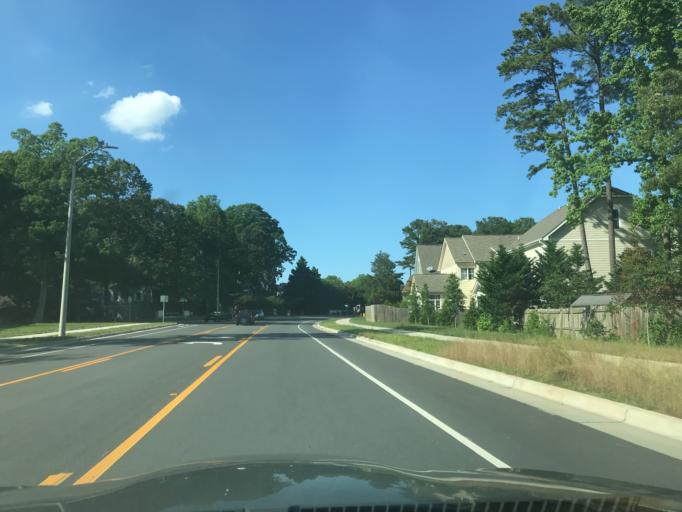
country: US
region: North Carolina
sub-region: Wake County
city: West Raleigh
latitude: 35.8660
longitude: -78.6347
